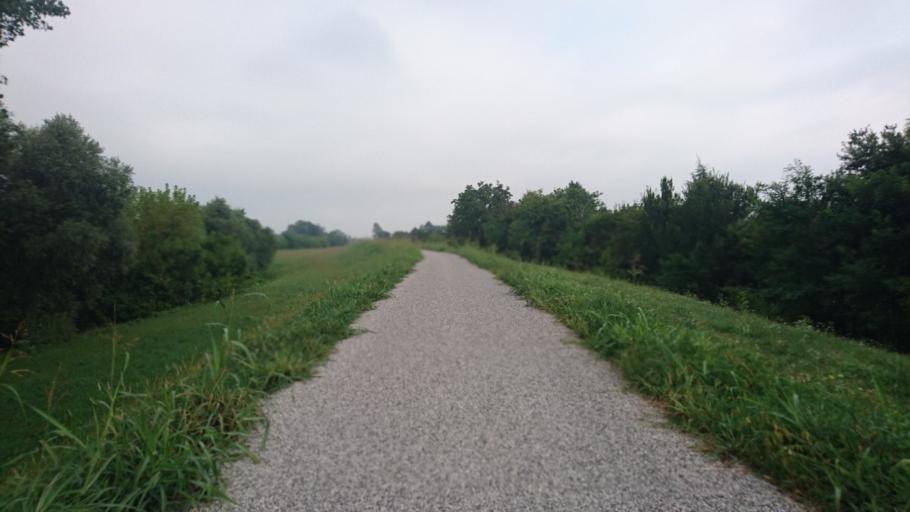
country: IT
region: Veneto
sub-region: Provincia di Padova
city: Saccolongo
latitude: 45.4118
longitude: 11.7474
